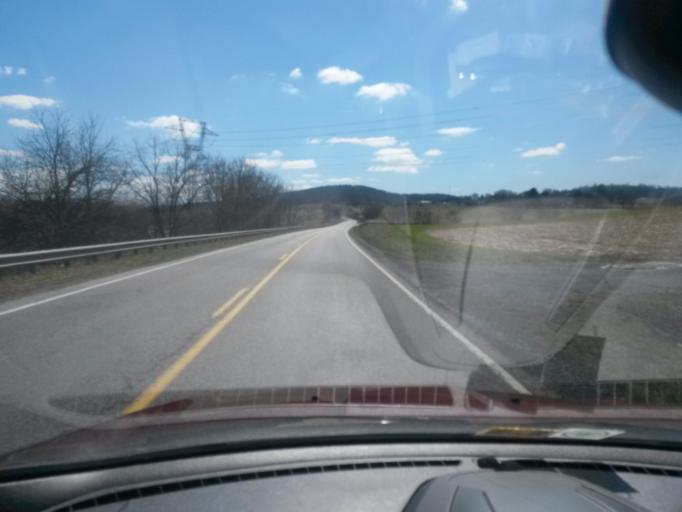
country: US
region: Virginia
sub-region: Augusta County
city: Jolivue
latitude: 38.0629
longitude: -79.0707
